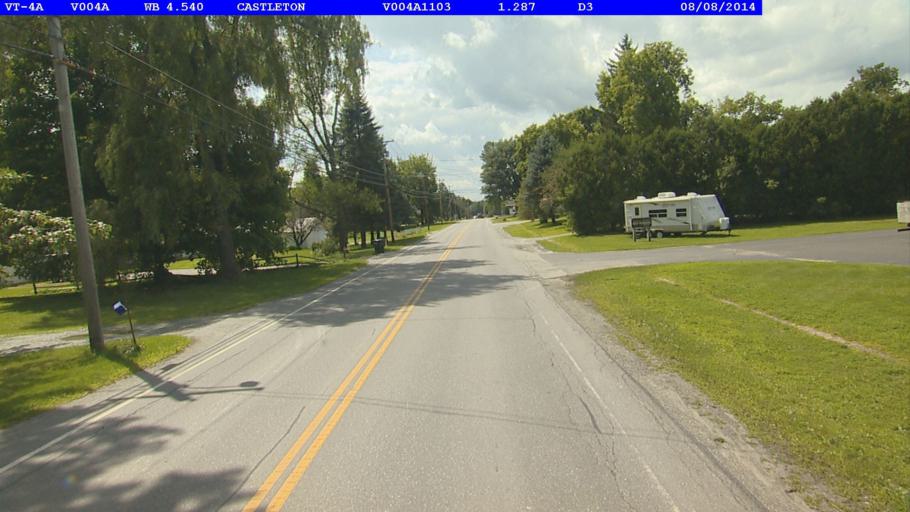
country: US
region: Vermont
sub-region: Rutland County
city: Castleton
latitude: 43.6080
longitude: -73.2187
